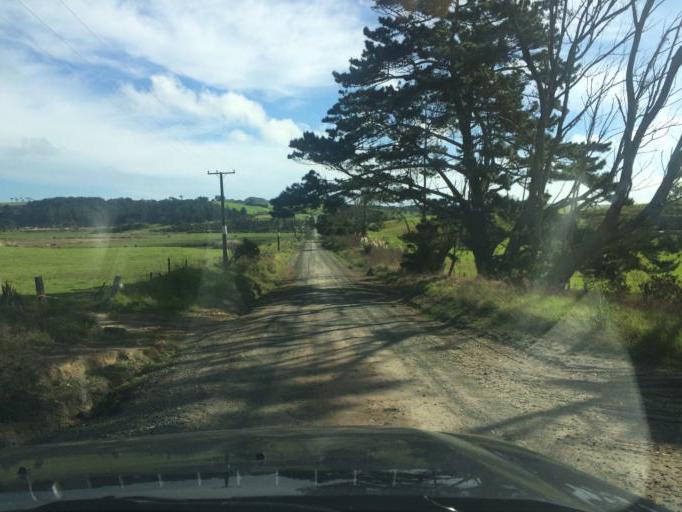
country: NZ
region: Northland
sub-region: Kaipara District
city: Dargaville
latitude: -36.0267
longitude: 173.8777
